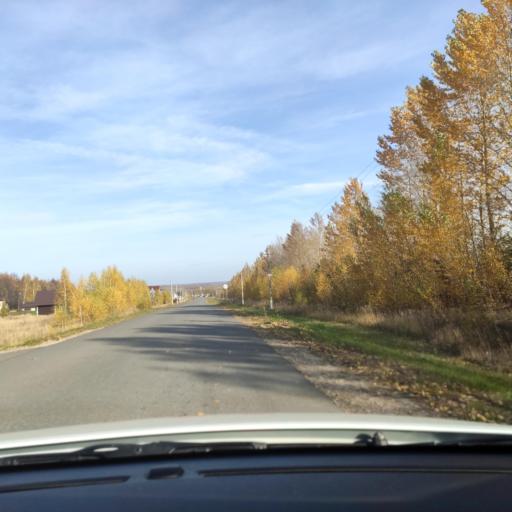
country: RU
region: Tatarstan
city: Pestretsy
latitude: 55.7268
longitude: 49.4590
